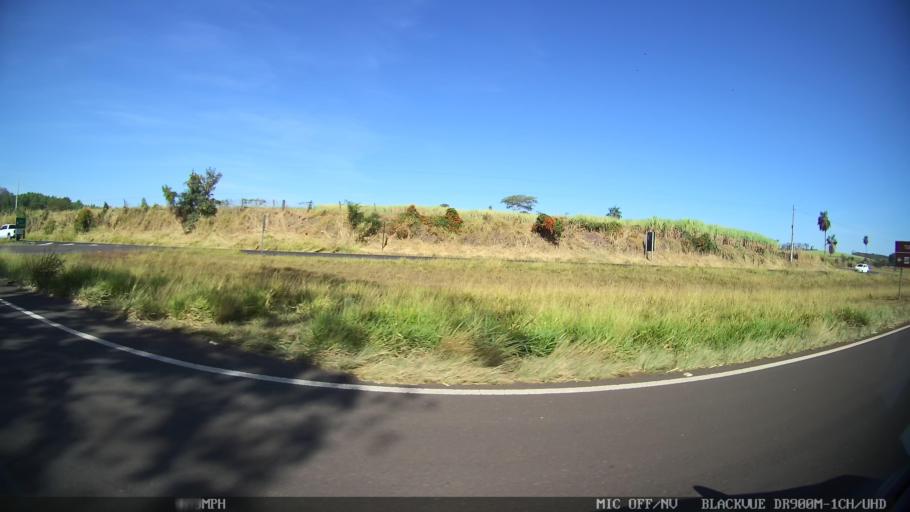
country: BR
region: Sao Paulo
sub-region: Olimpia
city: Olimpia
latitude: -20.6164
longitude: -48.7611
